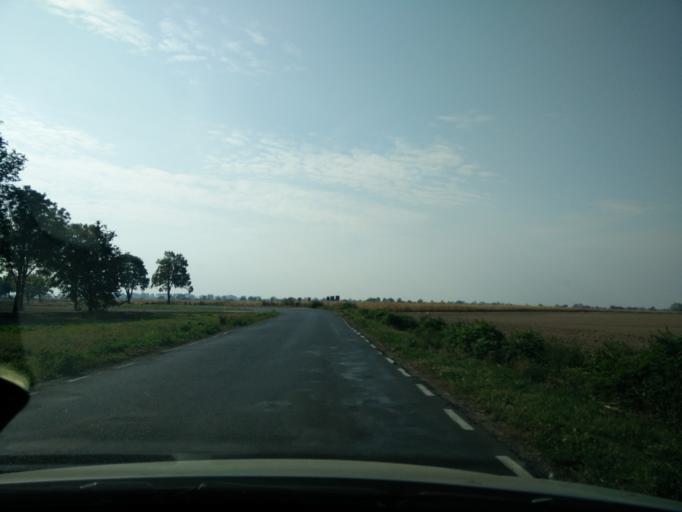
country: PL
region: Greater Poland Voivodeship
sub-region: Powiat sredzki
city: Sroda Wielkopolska
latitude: 52.2641
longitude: 17.3071
